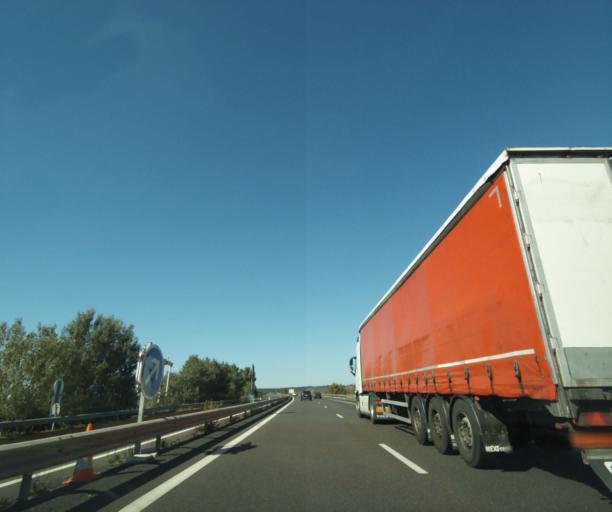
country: FR
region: Languedoc-Roussillon
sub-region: Departement du Gard
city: Bellegarde
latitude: 43.7200
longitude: 4.5089
